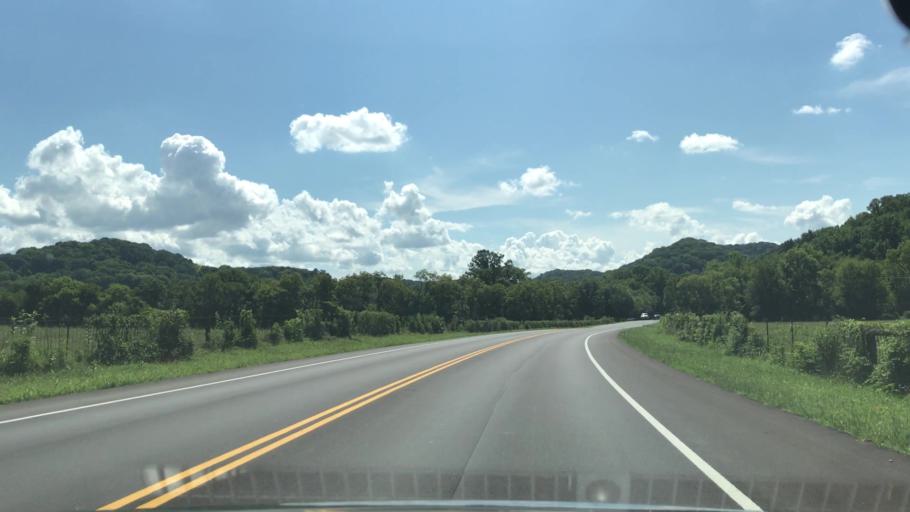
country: US
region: Tennessee
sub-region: Williamson County
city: Franklin
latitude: 35.9766
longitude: -86.8734
